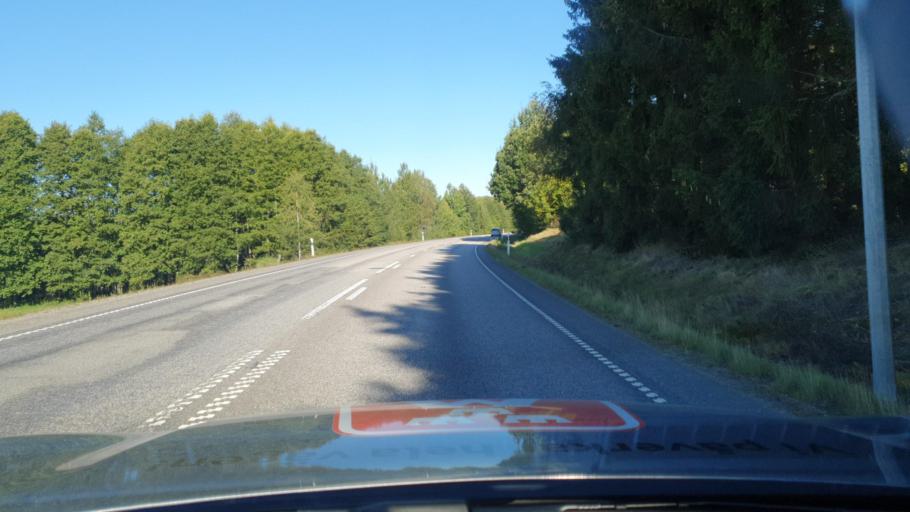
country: SE
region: OEstergoetland
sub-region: Linkopings Kommun
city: Ljungsbro
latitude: 58.7819
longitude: 15.5047
